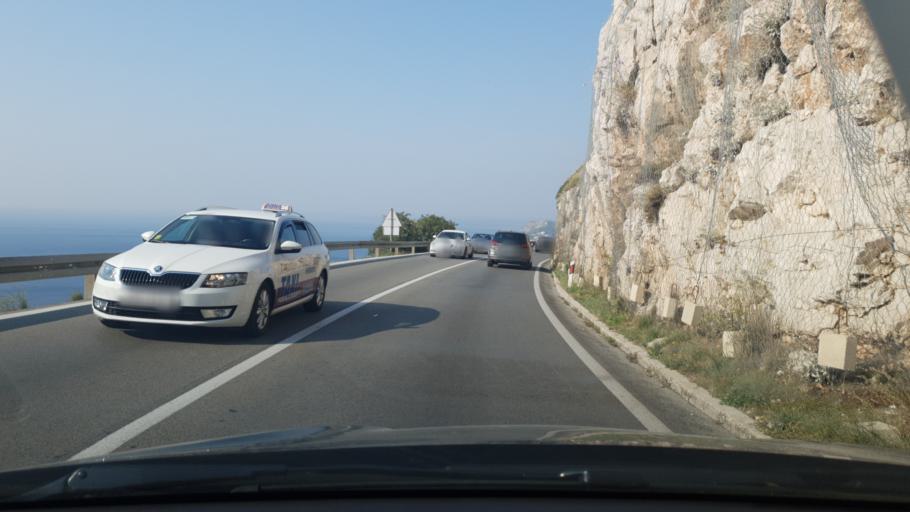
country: HR
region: Dubrovacko-Neretvanska
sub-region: Grad Dubrovnik
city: Dubrovnik
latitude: 42.6416
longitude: 18.1259
